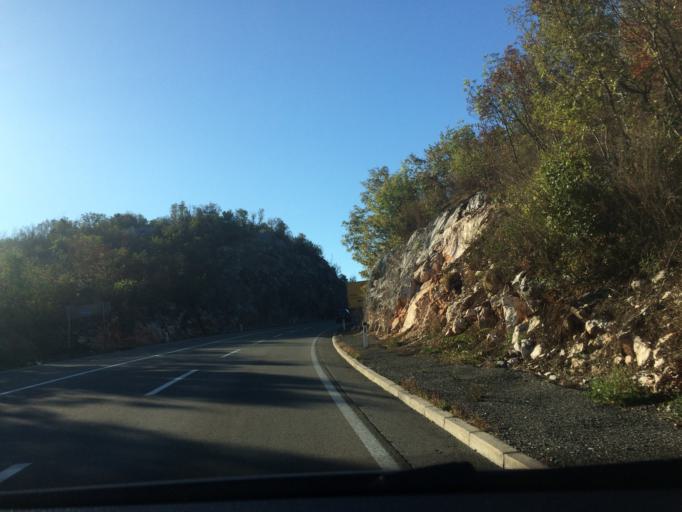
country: ME
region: Cetinje
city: Cetinje
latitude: 42.3798
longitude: 19.0591
